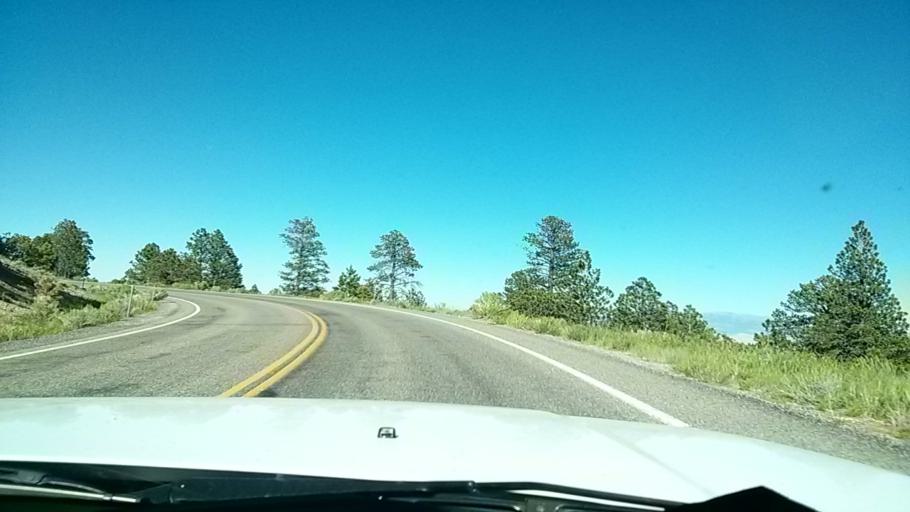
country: US
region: Utah
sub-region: Wayne County
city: Loa
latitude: 38.1099
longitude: -111.3319
